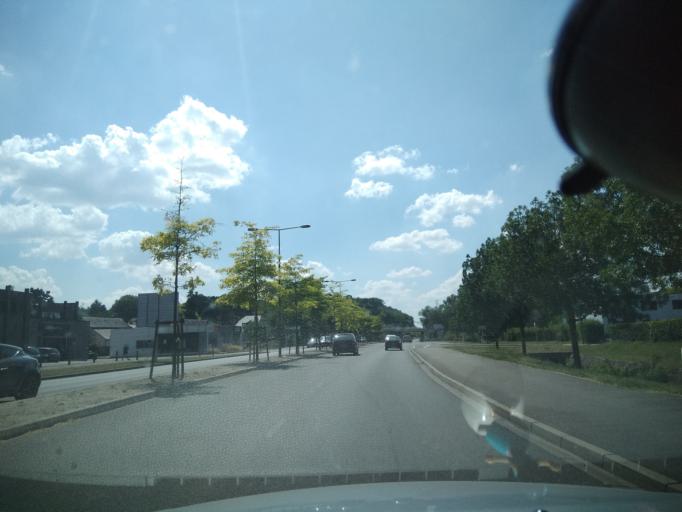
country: FR
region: Centre
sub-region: Departement d'Indre-et-Loire
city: Saint-Avertin
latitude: 47.3660
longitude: 0.7173
